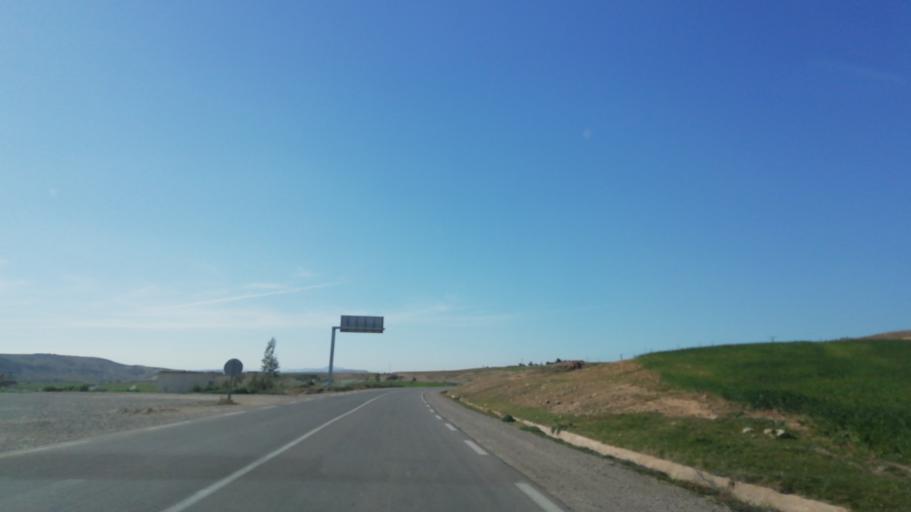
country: DZ
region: Mascara
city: Oued el Abtal
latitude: 35.4514
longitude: 0.7798
